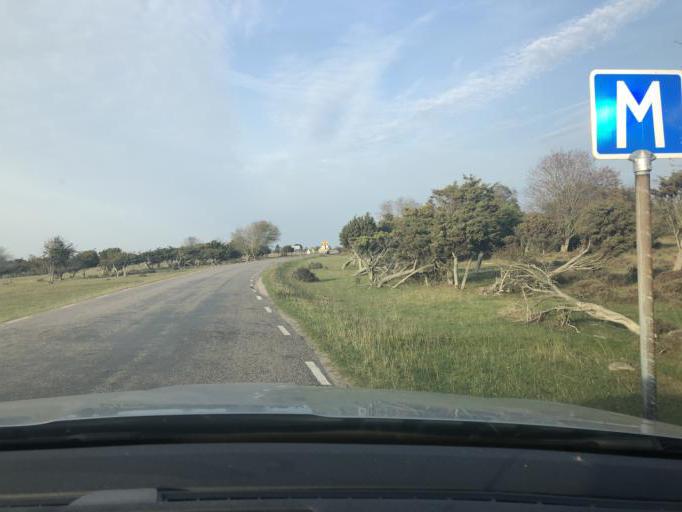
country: SE
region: Kalmar
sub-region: Morbylanga Kommun
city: Moerbylanga
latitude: 56.2167
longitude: 16.4084
